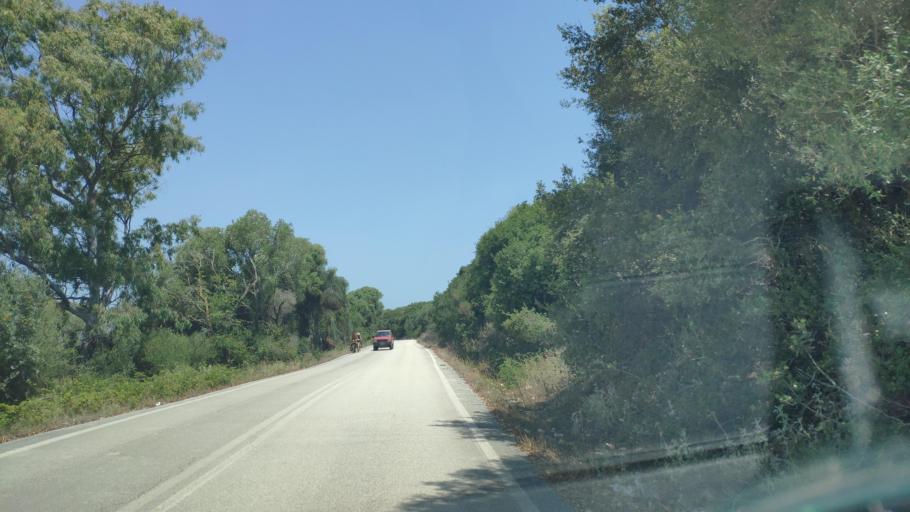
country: GR
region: Epirus
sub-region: Nomos Artas
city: Aneza
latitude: 39.0345
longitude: 20.8599
